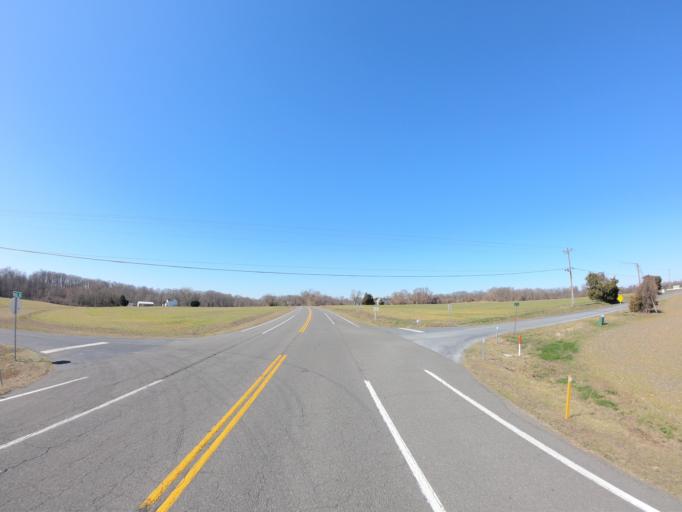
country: US
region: Delaware
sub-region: New Castle County
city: Townsend
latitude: 39.3437
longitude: -75.8581
